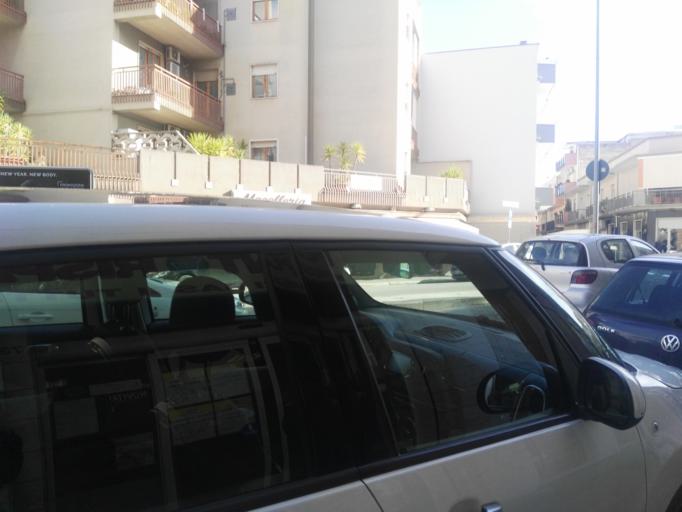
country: IT
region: Apulia
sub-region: Provincia di Barletta - Andria - Trani
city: Andria
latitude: 41.2275
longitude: 16.3063
